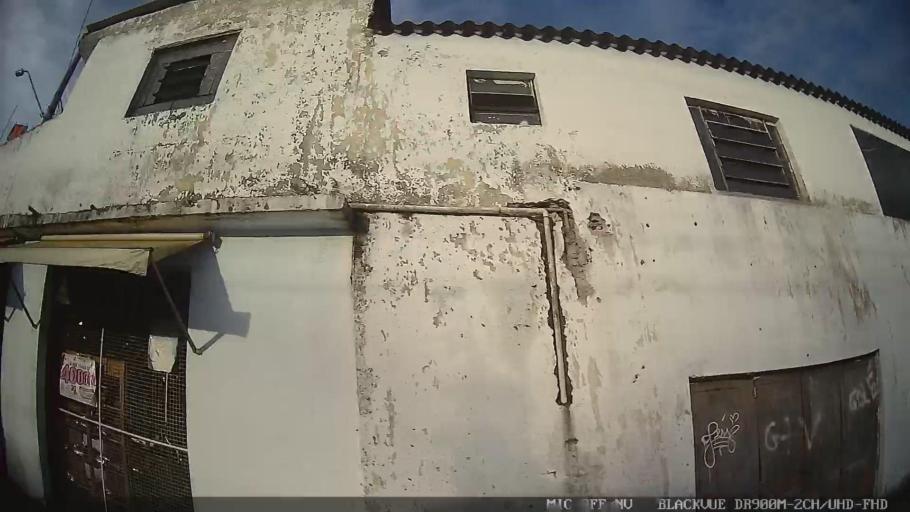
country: BR
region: Sao Paulo
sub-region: Mogi das Cruzes
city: Mogi das Cruzes
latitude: -23.5362
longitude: -46.1688
